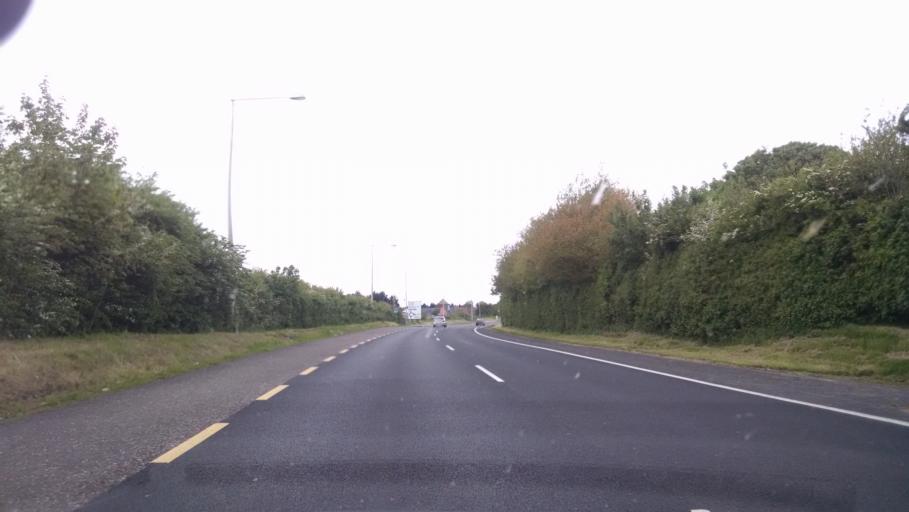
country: IE
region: Munster
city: Moyross
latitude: 52.6787
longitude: -8.6937
